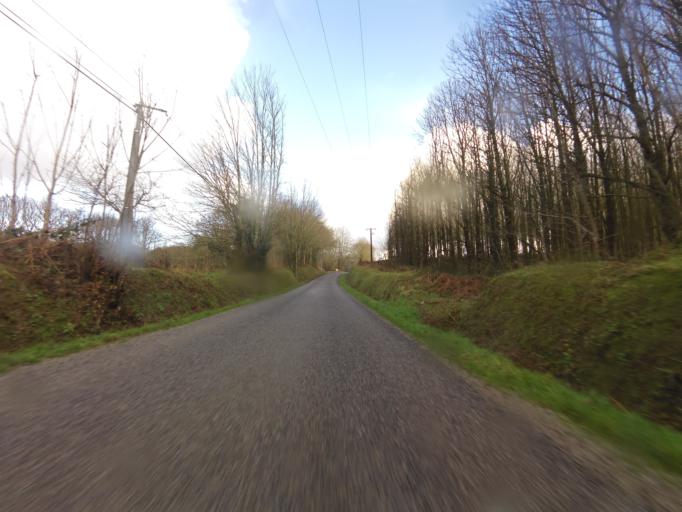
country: FR
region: Brittany
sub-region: Departement des Cotes-d'Armor
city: Rostrenen
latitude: 48.1772
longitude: -3.2900
